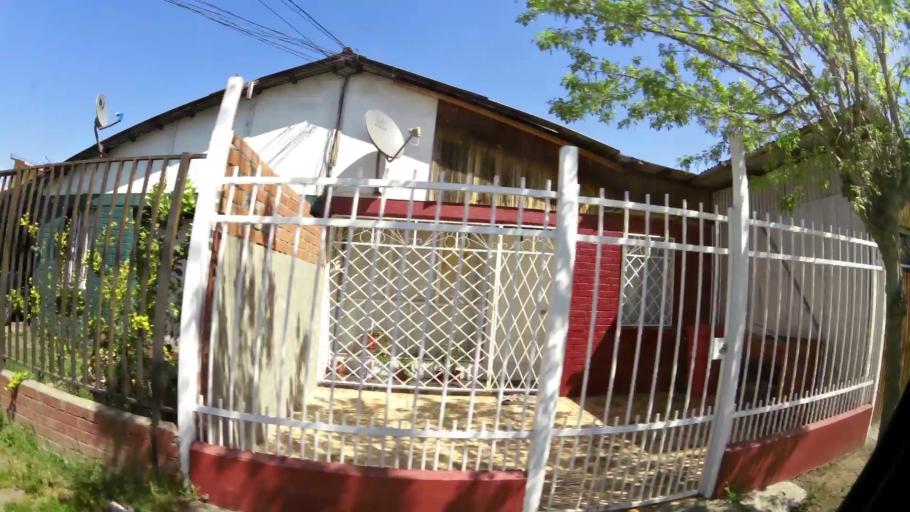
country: CL
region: Santiago Metropolitan
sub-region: Provincia de Talagante
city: Talagante
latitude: -33.6551
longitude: -70.9127
